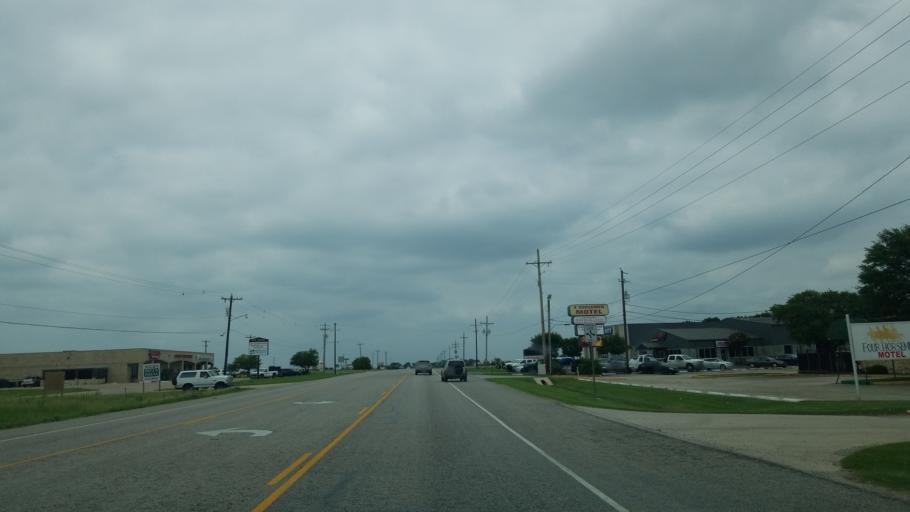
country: US
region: Texas
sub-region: Denton County
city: Pilot Point
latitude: 33.4083
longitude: -96.9420
